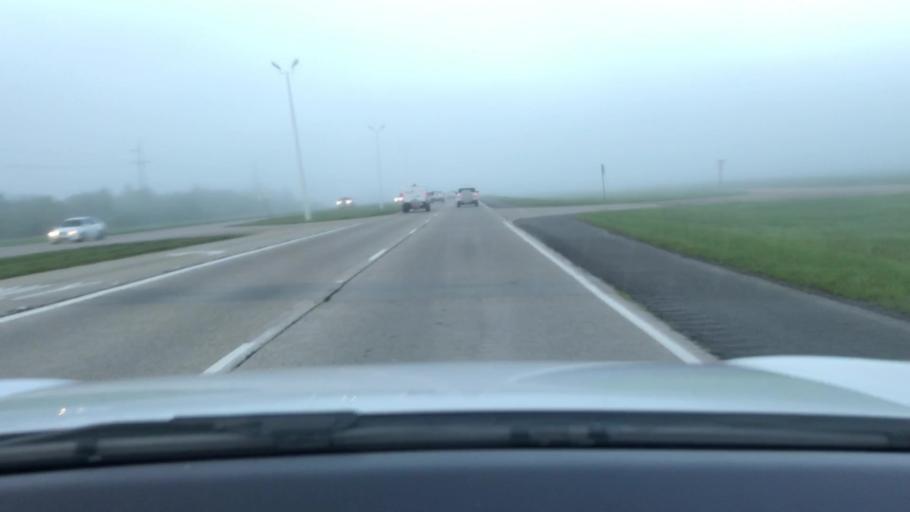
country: US
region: Louisiana
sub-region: West Baton Rouge Parish
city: Addis
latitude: 30.3472
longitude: -91.2588
